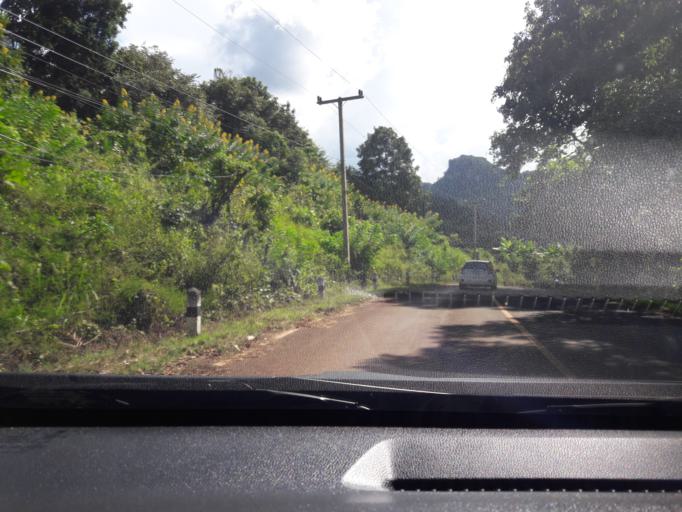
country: TH
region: Mae Hong Son
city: Sop Pong
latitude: 19.5660
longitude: 98.1974
